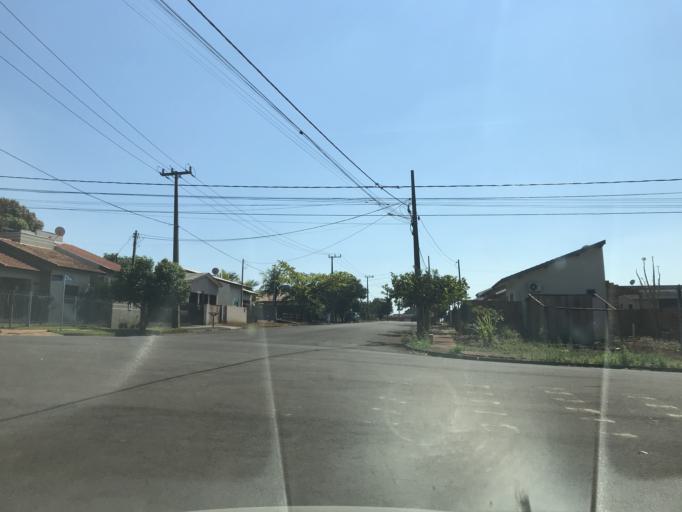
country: BR
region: Parana
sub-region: Palotina
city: Palotina
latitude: -24.2994
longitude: -53.8310
